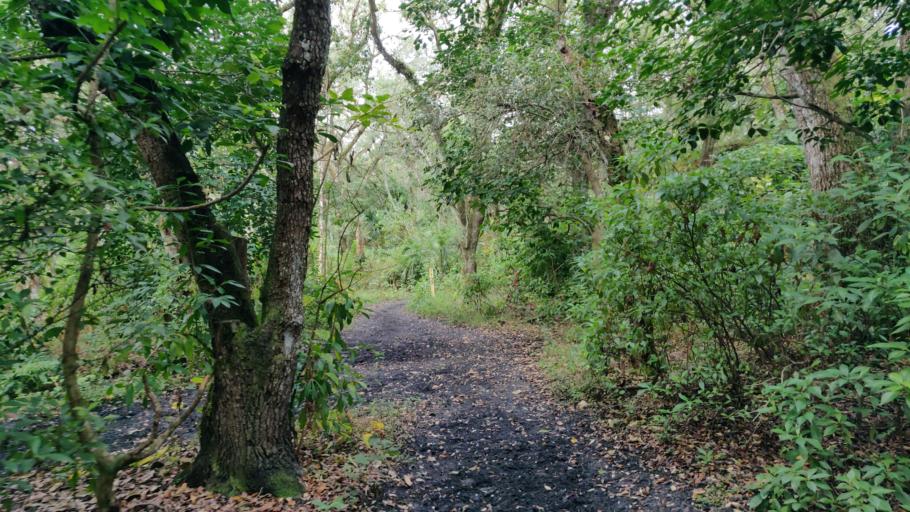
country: US
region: Florida
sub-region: Broward County
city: Cooper City
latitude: 26.0751
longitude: -80.2746
